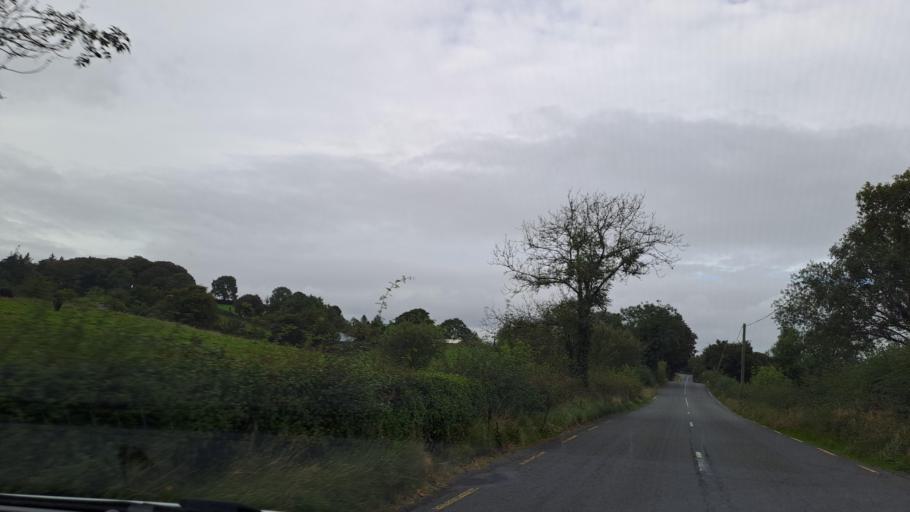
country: IE
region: Ulster
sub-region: An Cabhan
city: Bailieborough
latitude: 54.0346
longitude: -6.8975
